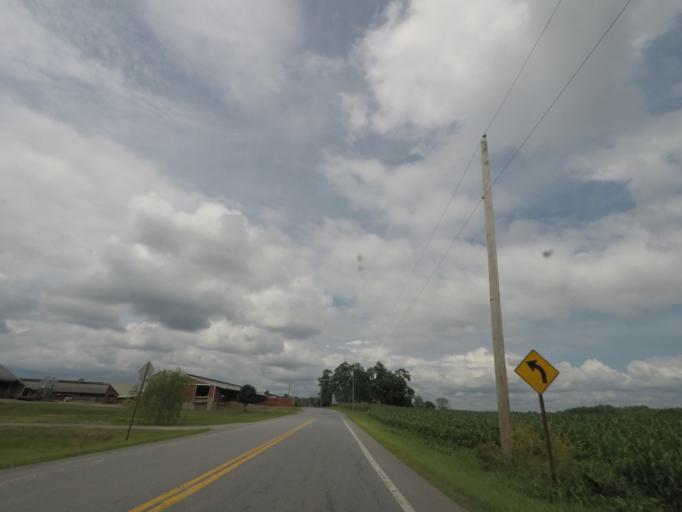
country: US
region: New York
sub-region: Saratoga County
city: Saratoga Springs
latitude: 43.0623
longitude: -73.6838
